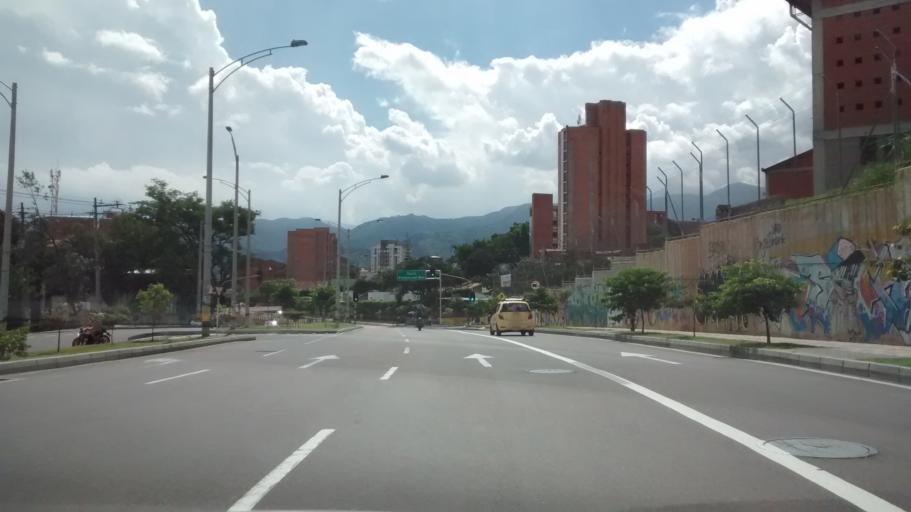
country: CO
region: Antioquia
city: Medellin
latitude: 6.2821
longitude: -75.5860
